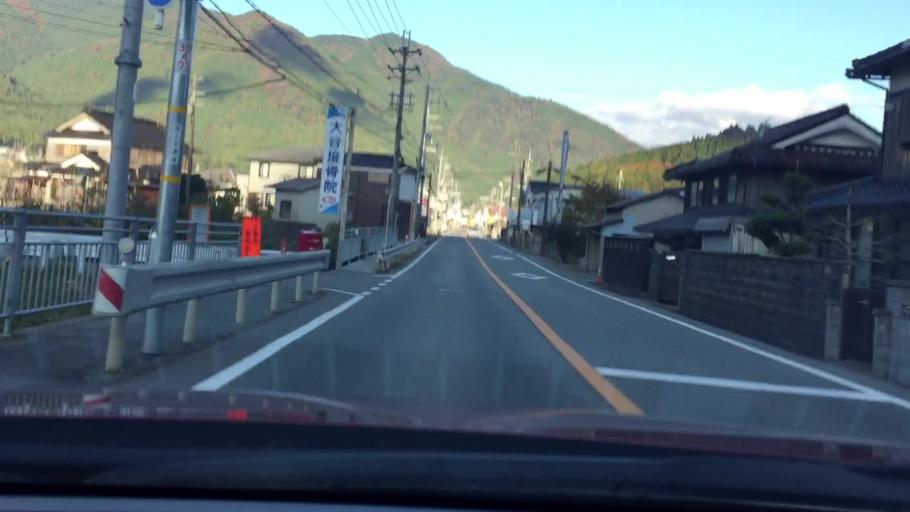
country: JP
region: Hyogo
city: Yamazakicho-nakabirose
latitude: 35.1081
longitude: 134.5800
